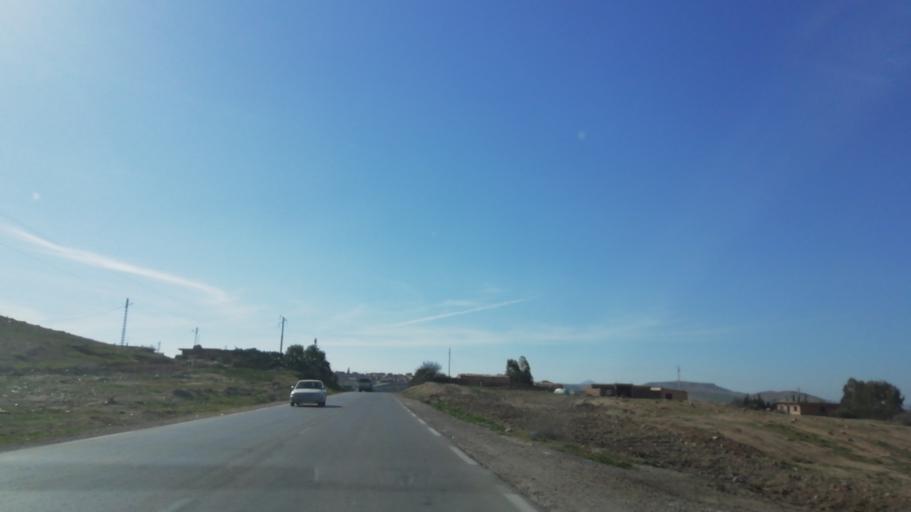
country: DZ
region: Mascara
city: Oued el Abtal
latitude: 35.4555
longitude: 0.7274
